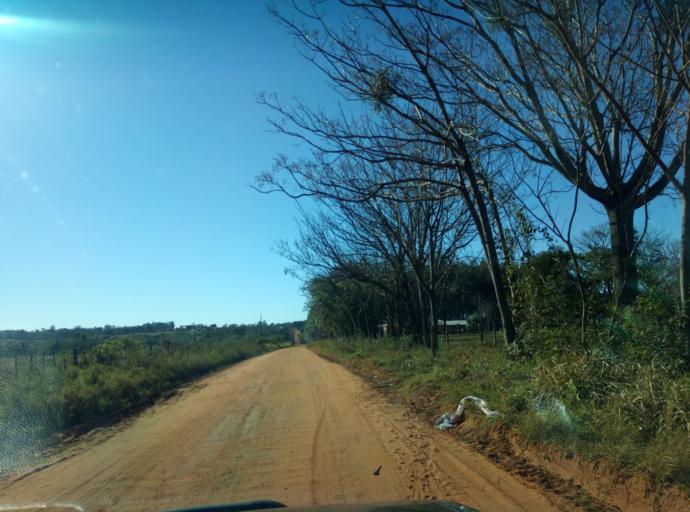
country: PY
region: Caaguazu
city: Doctor Cecilio Baez
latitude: -25.1629
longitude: -56.2634
